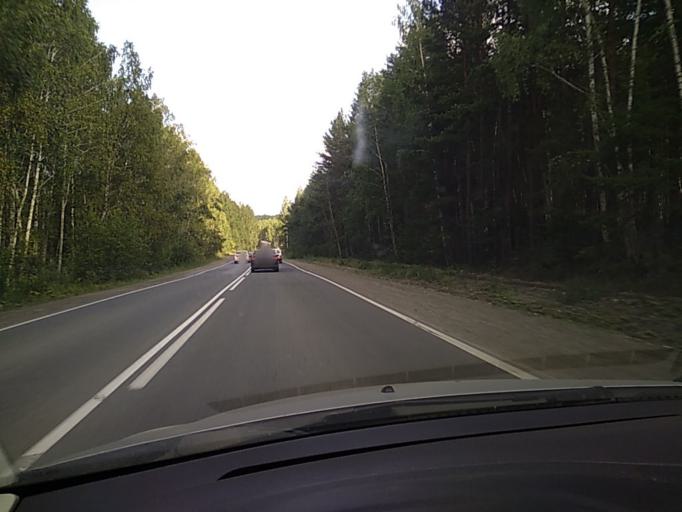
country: RU
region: Chelyabinsk
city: Karabash
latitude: 55.5003
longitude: 60.2906
